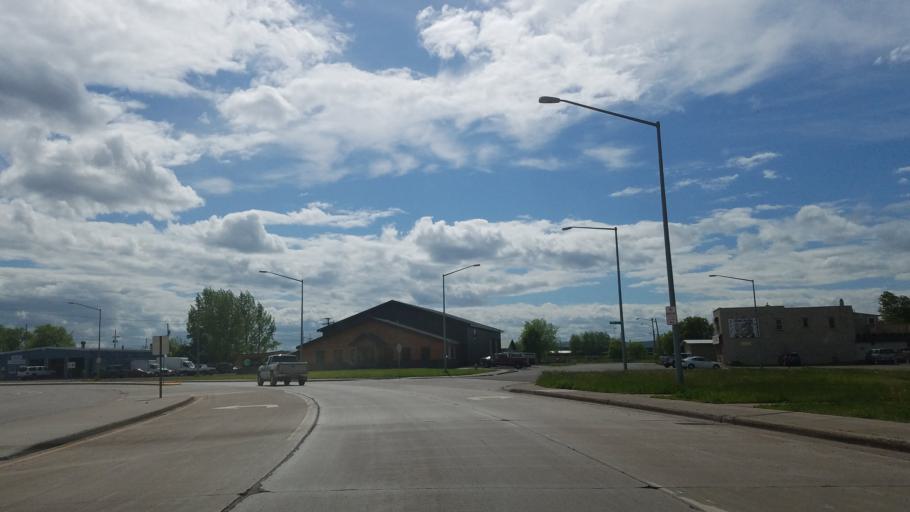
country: US
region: Wisconsin
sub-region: Douglas County
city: Superior
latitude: 46.7352
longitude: -92.1025
